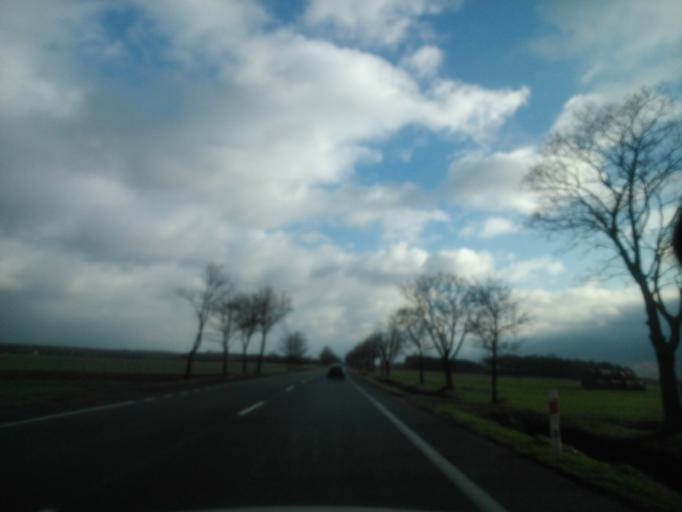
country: PL
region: Masovian Voivodeship
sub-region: Powiat sierpecki
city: Zawidz
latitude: 52.8041
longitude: 19.8466
